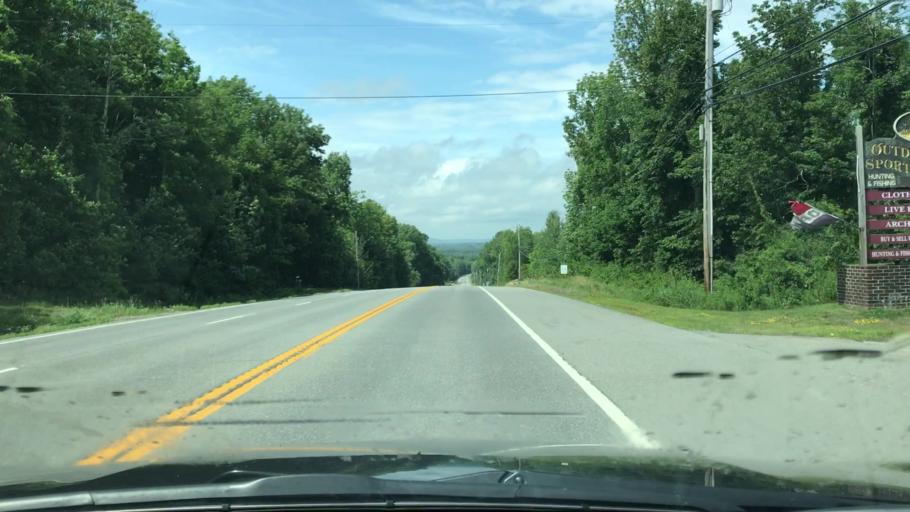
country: US
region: Maine
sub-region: Waldo County
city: Northport
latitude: 44.3614
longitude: -68.9757
